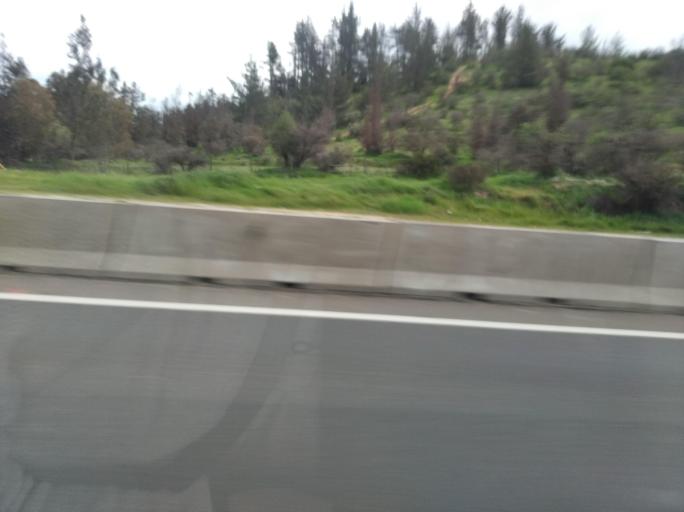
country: CL
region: Valparaiso
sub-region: Provincia de Marga Marga
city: Quilpue
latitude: -33.2631
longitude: -71.4351
